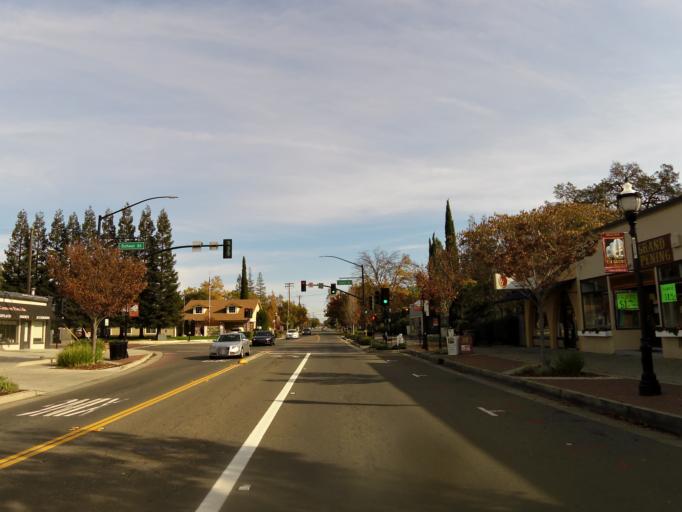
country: US
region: California
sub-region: Sacramento County
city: Elk Grove
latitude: 38.4090
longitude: -121.3630
